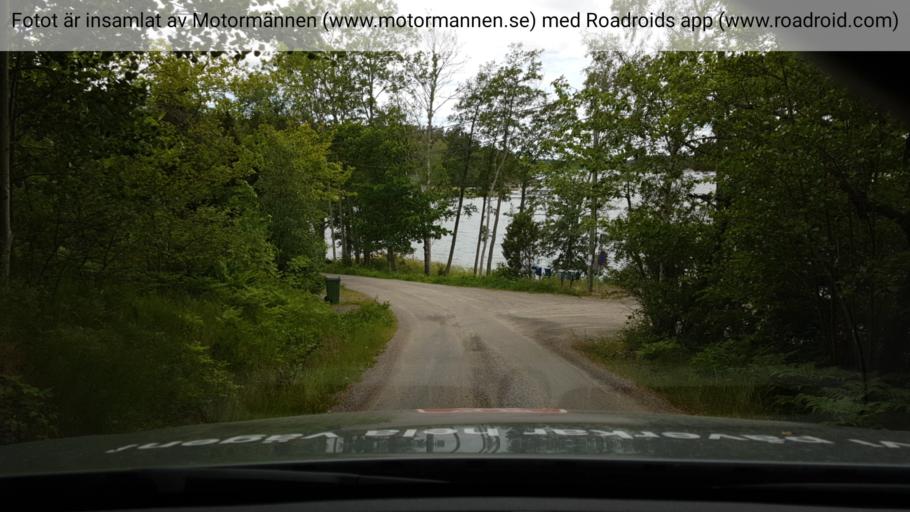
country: SE
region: Stockholm
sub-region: Haninge Kommun
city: Jordbro
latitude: 59.0186
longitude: 18.0947
